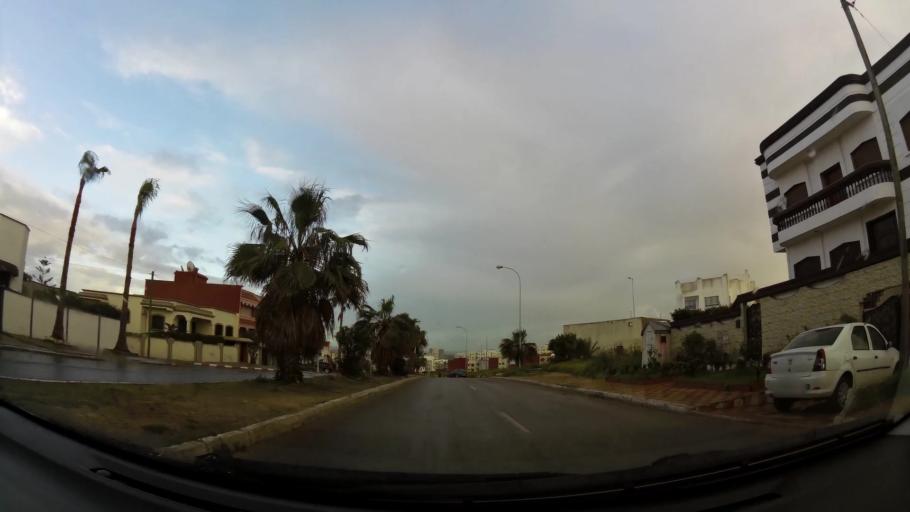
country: MA
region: Doukkala-Abda
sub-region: El-Jadida
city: El Jadida
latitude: 33.2294
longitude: -8.4971
